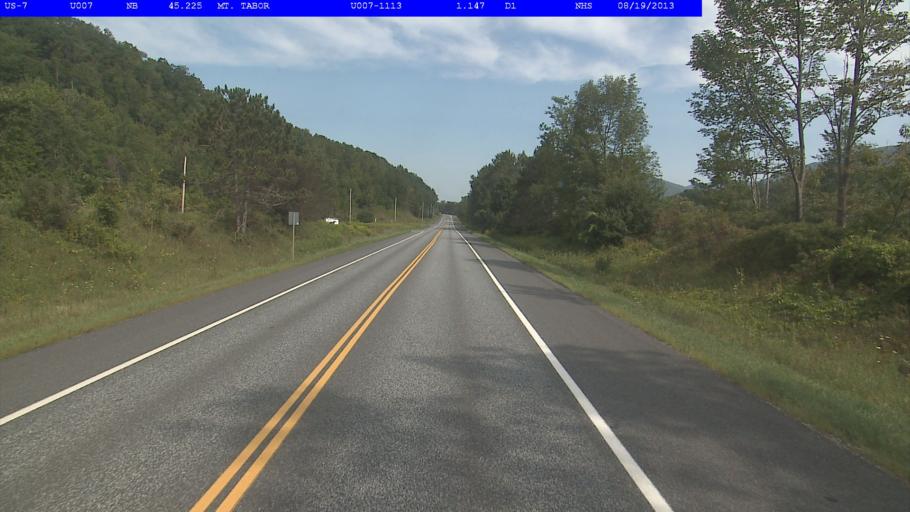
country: US
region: Vermont
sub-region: Bennington County
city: Manchester Center
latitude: 43.3214
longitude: -72.9911
